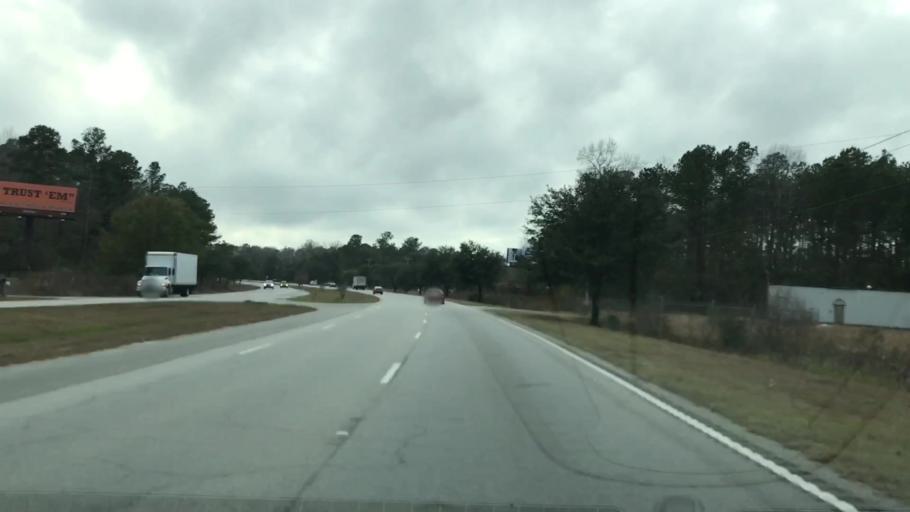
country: US
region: South Carolina
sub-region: Berkeley County
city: Moncks Corner
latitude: 33.1844
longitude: -80.0135
